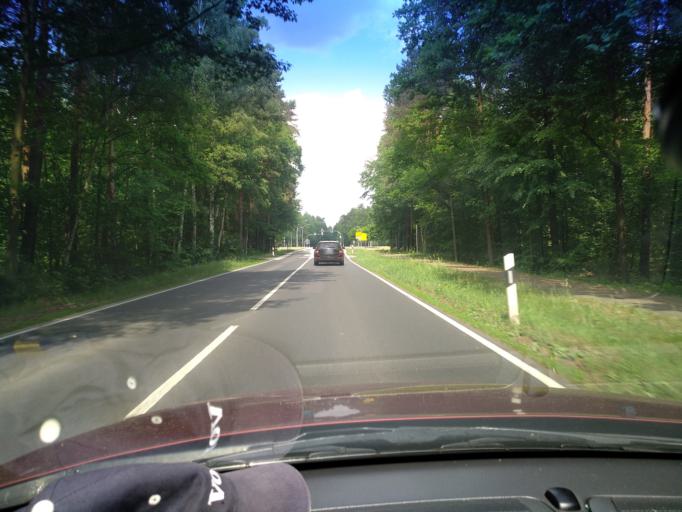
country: DE
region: Saxony
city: Niesky
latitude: 51.2926
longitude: 14.8095
